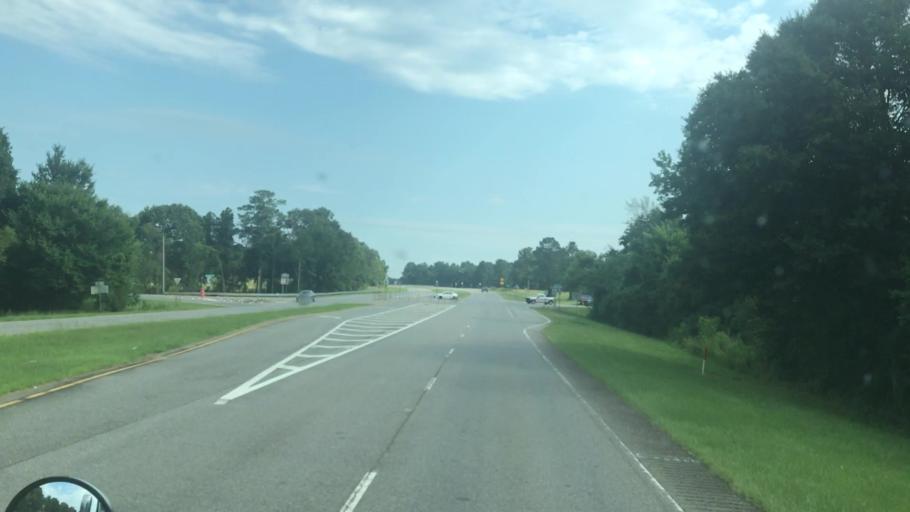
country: US
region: Georgia
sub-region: Early County
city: Blakely
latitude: 31.3794
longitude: -84.9213
